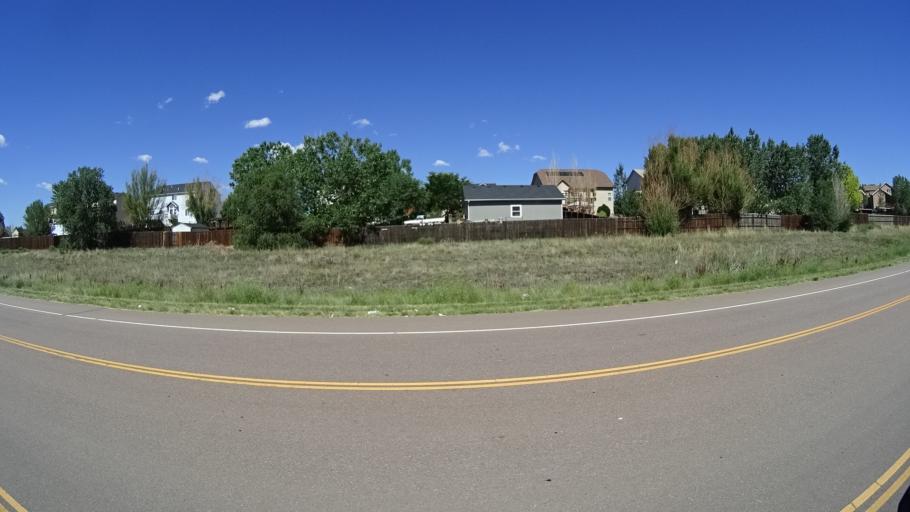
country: US
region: Colorado
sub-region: El Paso County
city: Security-Widefield
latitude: 38.7395
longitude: -104.6491
